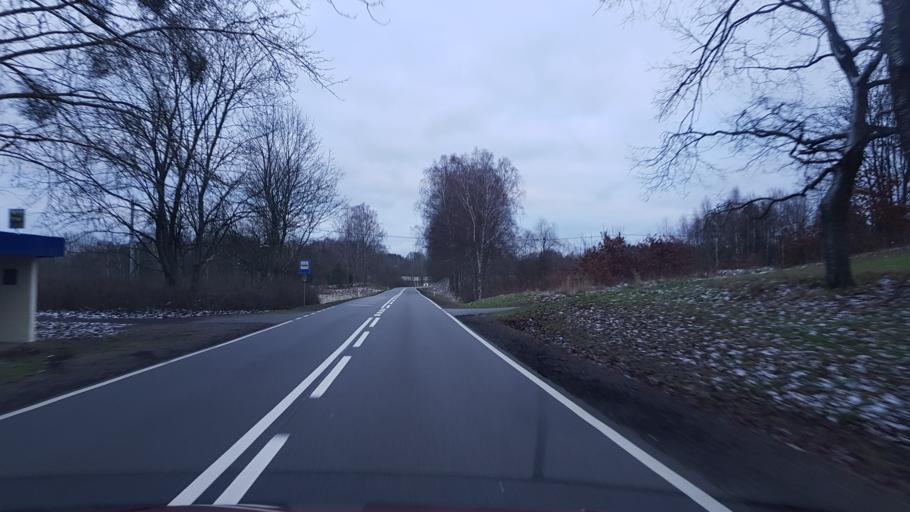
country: PL
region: Pomeranian Voivodeship
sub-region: Powiat bytowski
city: Tuchomie
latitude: 54.0500
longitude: 17.2167
